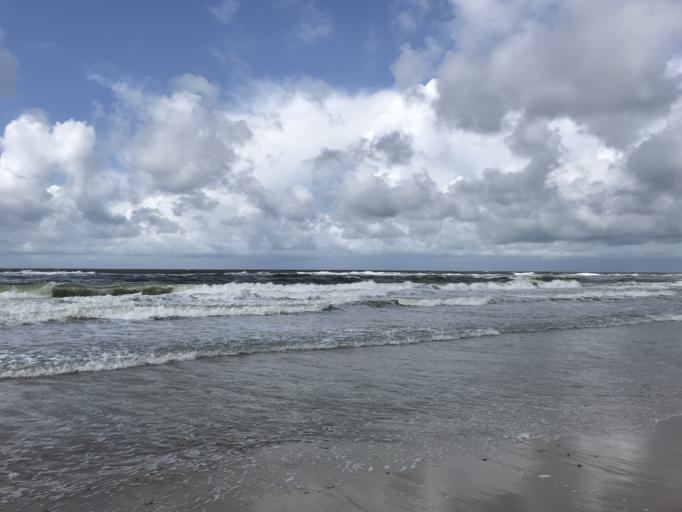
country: DK
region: Central Jutland
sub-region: Ringkobing-Skjern Kommune
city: Hvide Sande
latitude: 56.1197
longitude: 8.1078
